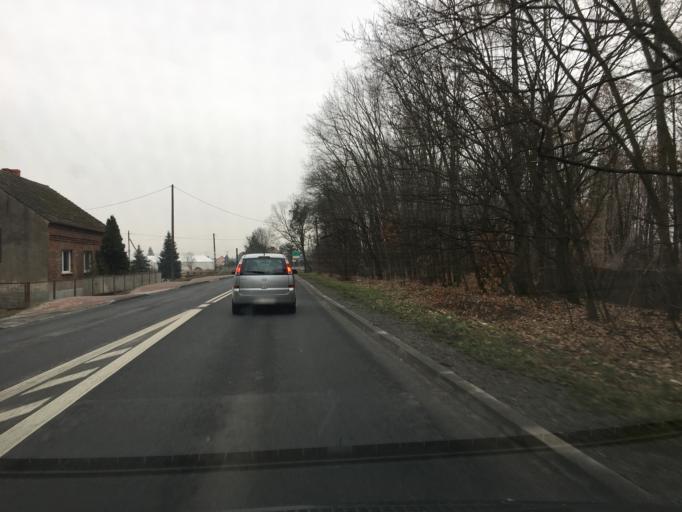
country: PL
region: Opole Voivodeship
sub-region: Powiat kedzierzynsko-kozielski
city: Kedzierzyn-Kozle
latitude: 50.3193
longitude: 18.2225
